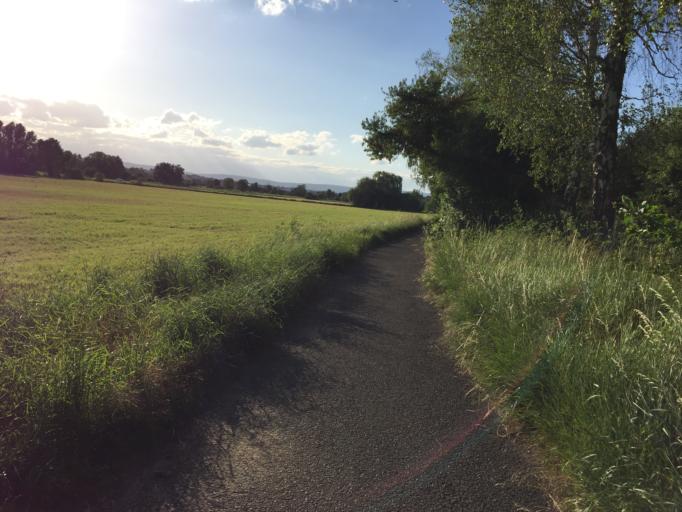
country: DE
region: Hesse
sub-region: Regierungsbezirk Darmstadt
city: Karben
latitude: 50.2159
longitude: 8.7791
